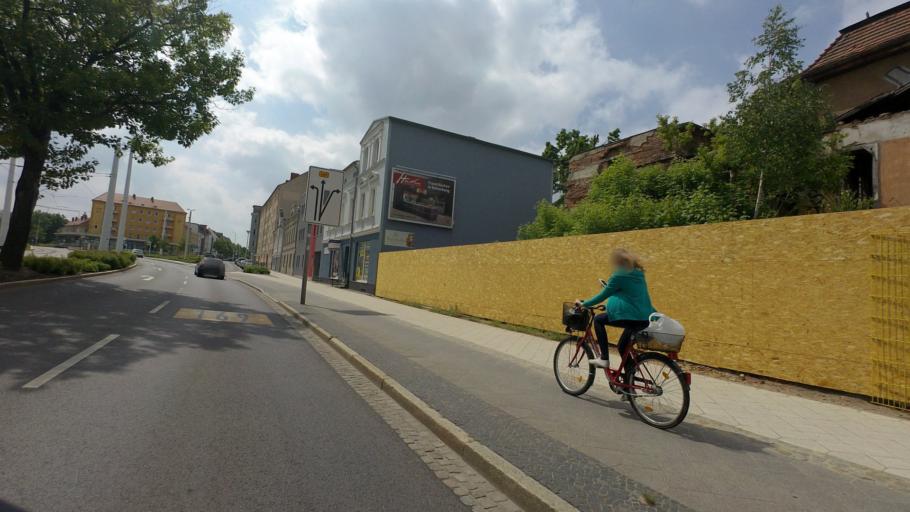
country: DE
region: Brandenburg
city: Cottbus
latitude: 51.7458
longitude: 14.3313
